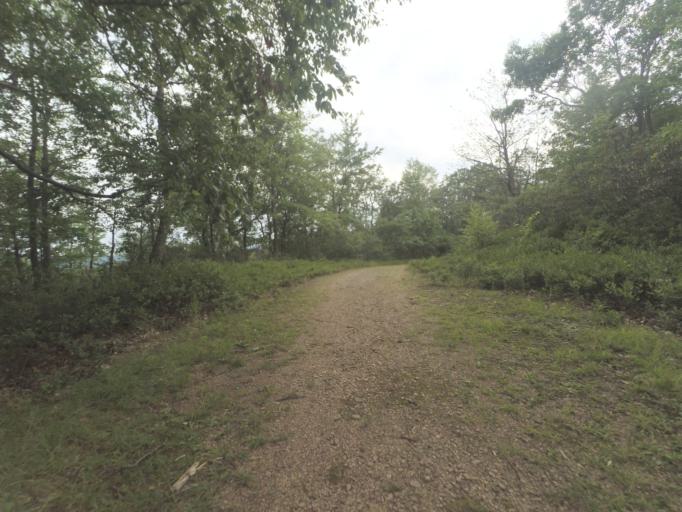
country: US
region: Pennsylvania
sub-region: Centre County
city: Boalsburg
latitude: 40.7175
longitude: -77.7772
